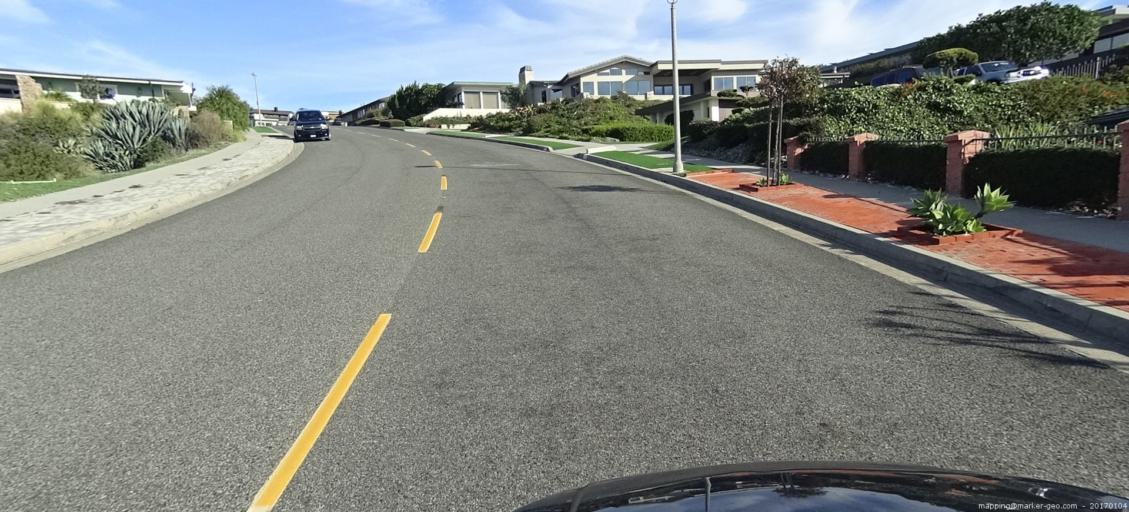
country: US
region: California
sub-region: Orange County
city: Dana Point
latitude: 33.4903
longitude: -117.7250
